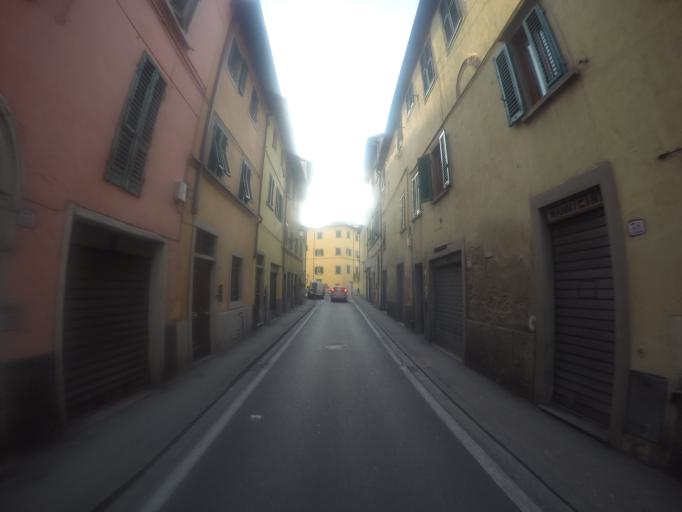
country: IT
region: Tuscany
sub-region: Provincia di Prato
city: Prato
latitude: 43.8824
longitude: 11.0994
